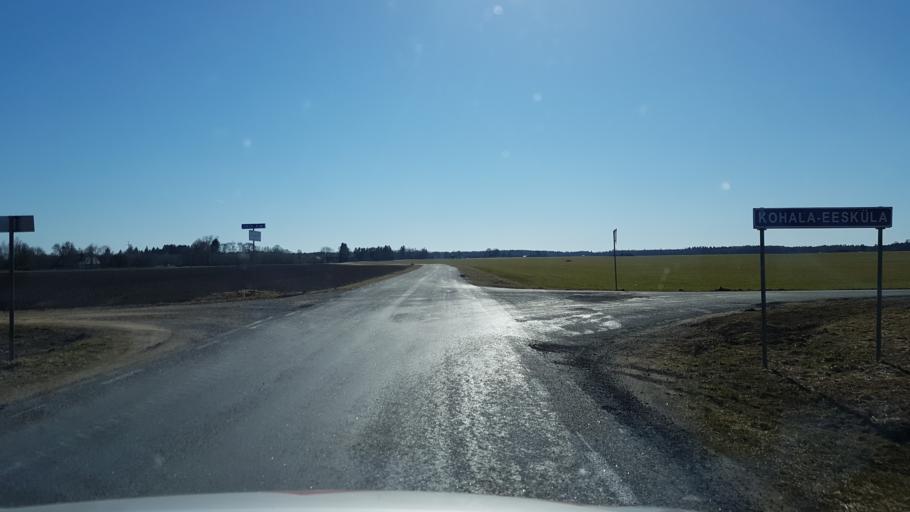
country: EE
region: Laeaene-Virumaa
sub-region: Viru-Nigula vald
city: Kunda
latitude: 59.4036
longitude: 26.5176
